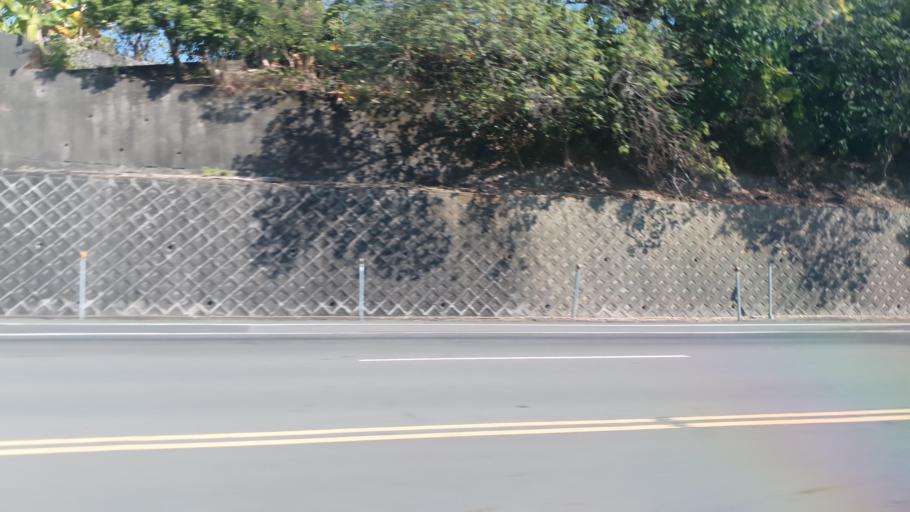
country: TW
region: Taiwan
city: Yujing
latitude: 23.0575
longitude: 120.3975
